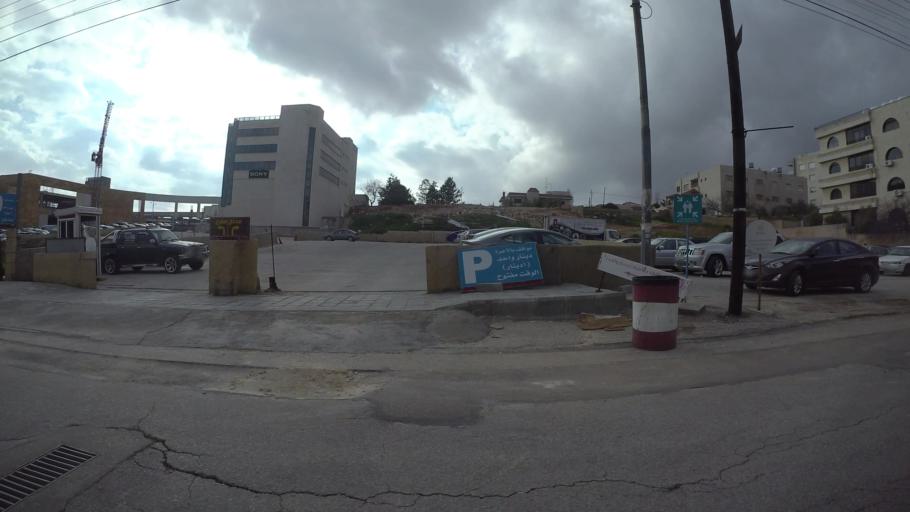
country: JO
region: Amman
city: Wadi as Sir
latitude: 31.9786
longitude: 35.8434
